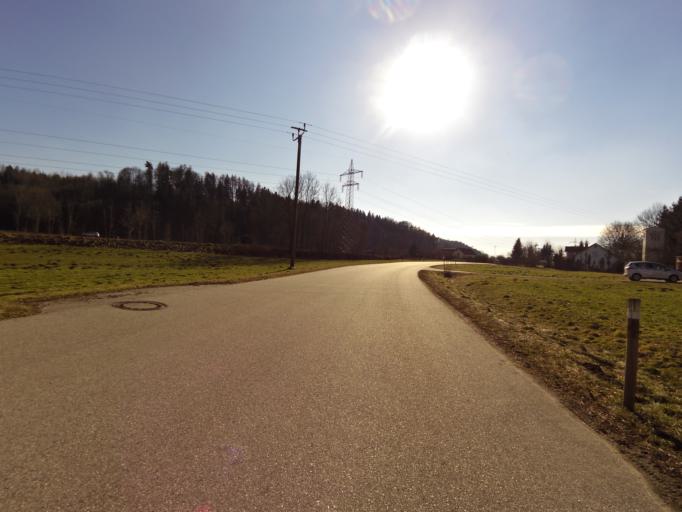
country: DE
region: Bavaria
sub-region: Lower Bavaria
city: Eching
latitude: 48.4982
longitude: 12.0453
